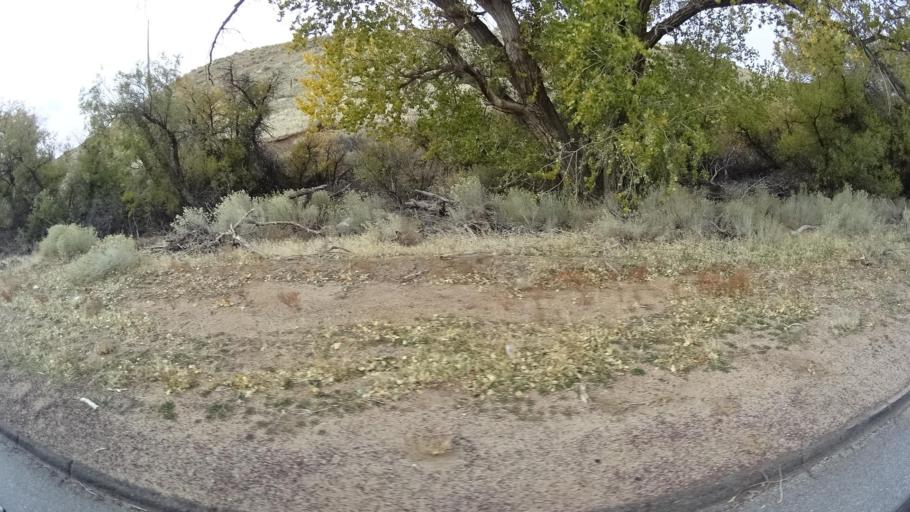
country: US
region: California
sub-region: Kern County
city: Tehachapi
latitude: 35.0685
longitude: -118.3959
